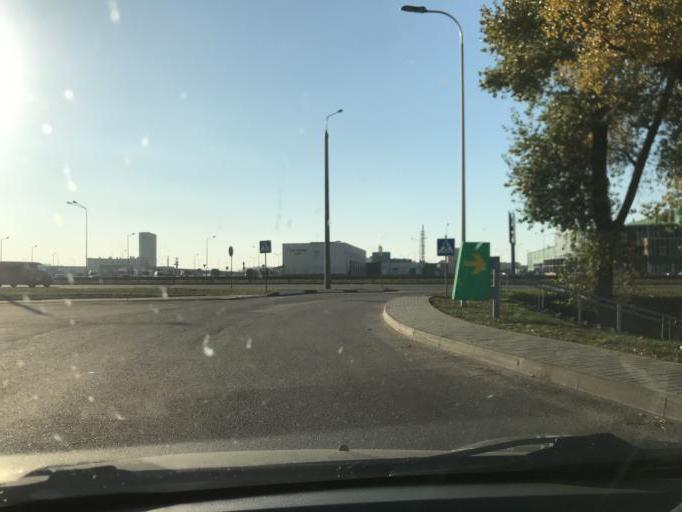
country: BY
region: Minsk
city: Yubilyeyny
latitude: 53.8121
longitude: 27.5311
